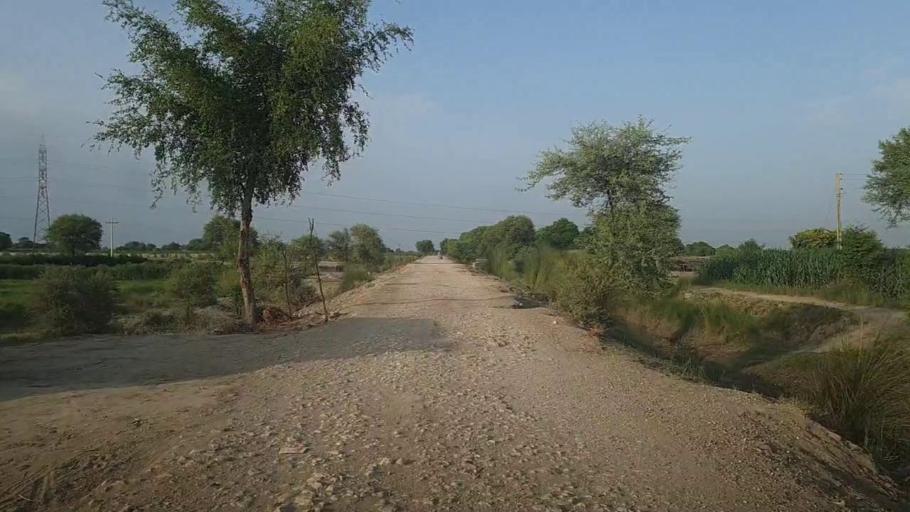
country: PK
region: Sindh
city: Ubauro
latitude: 28.3655
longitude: 69.7949
